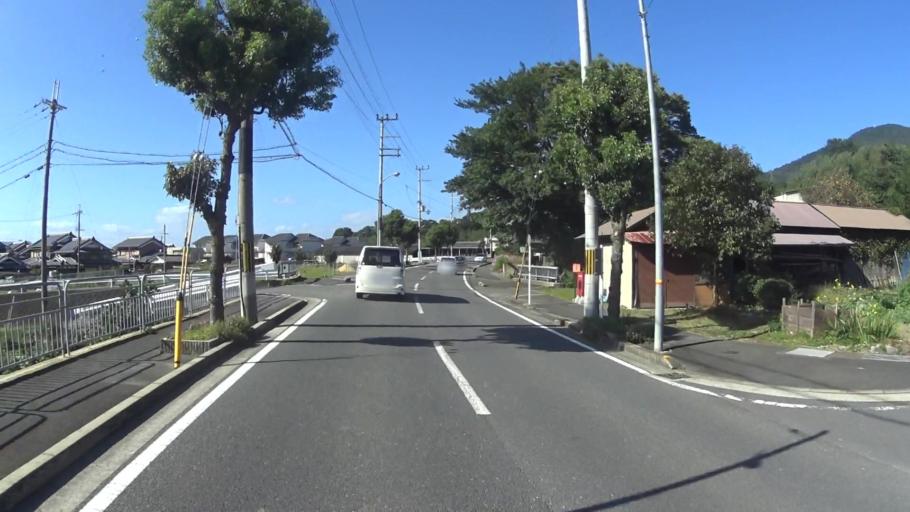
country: JP
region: Kyoto
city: Kameoka
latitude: 35.0272
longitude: 135.5874
